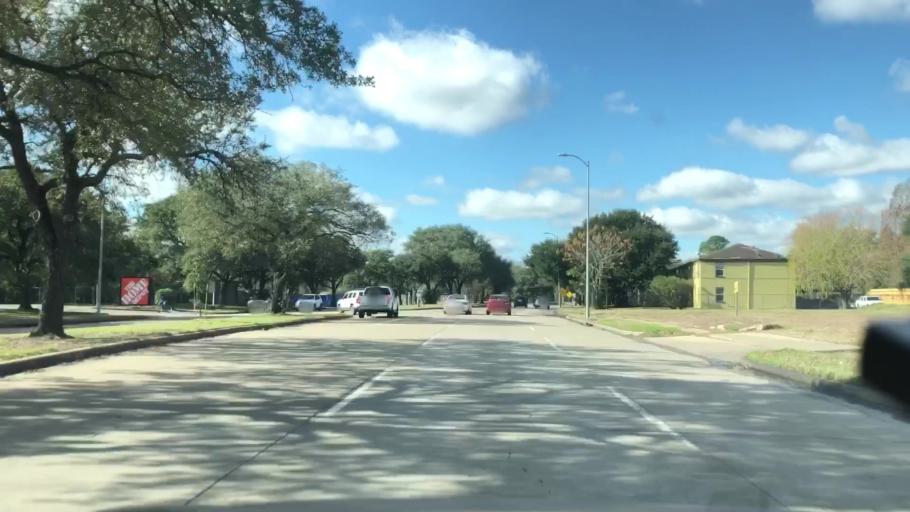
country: US
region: Texas
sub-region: Harris County
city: Bellaire
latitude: 29.6583
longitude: -95.4792
